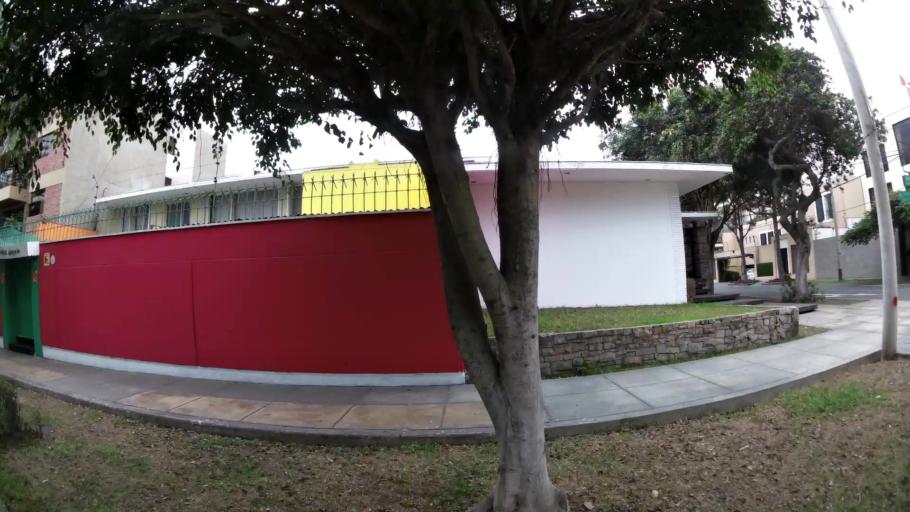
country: PE
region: Lima
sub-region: Lima
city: Surco
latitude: -12.1214
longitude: -77.0147
